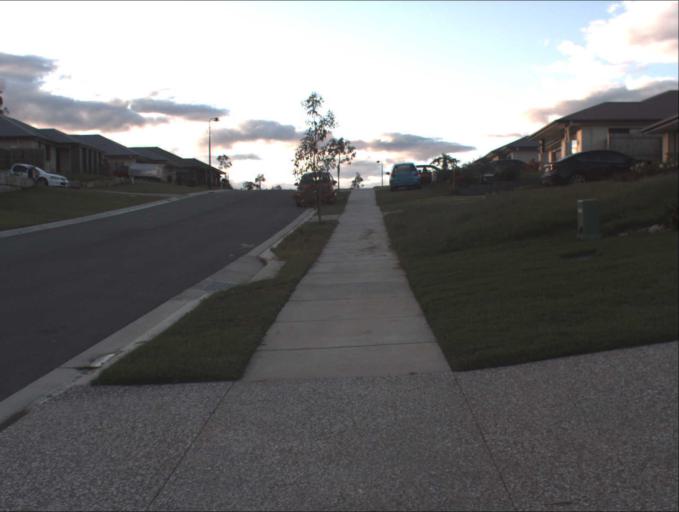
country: AU
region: Queensland
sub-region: Logan
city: North Maclean
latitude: -27.8008
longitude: 152.9549
